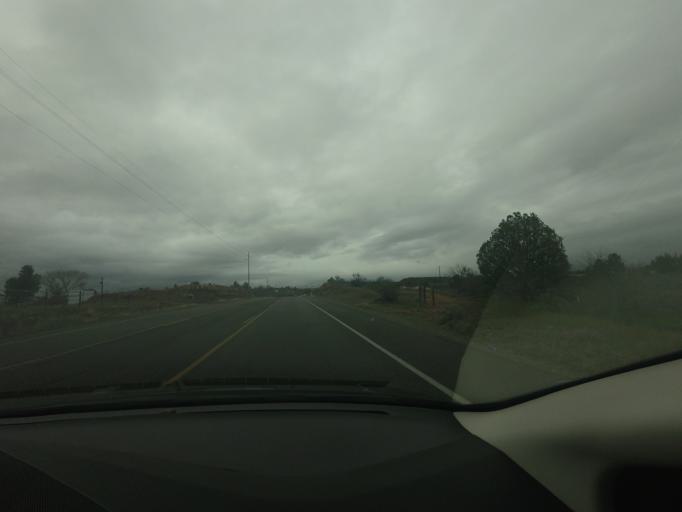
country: US
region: Arizona
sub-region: Yavapai County
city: Lake Montezuma
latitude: 34.6468
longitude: -111.7852
